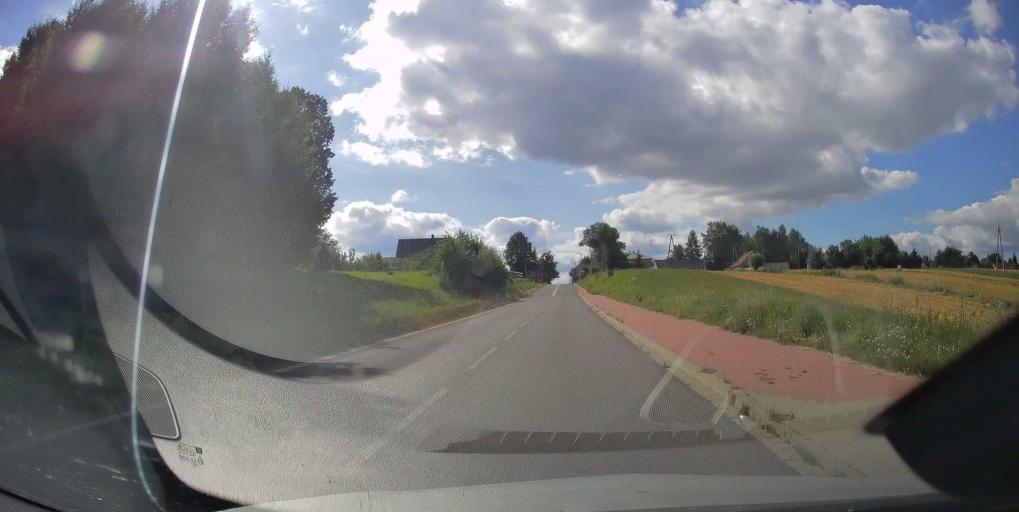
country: PL
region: Swietokrzyskie
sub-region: Powiat kielecki
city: Nowa Slupia
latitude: 50.8826
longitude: 21.0545
